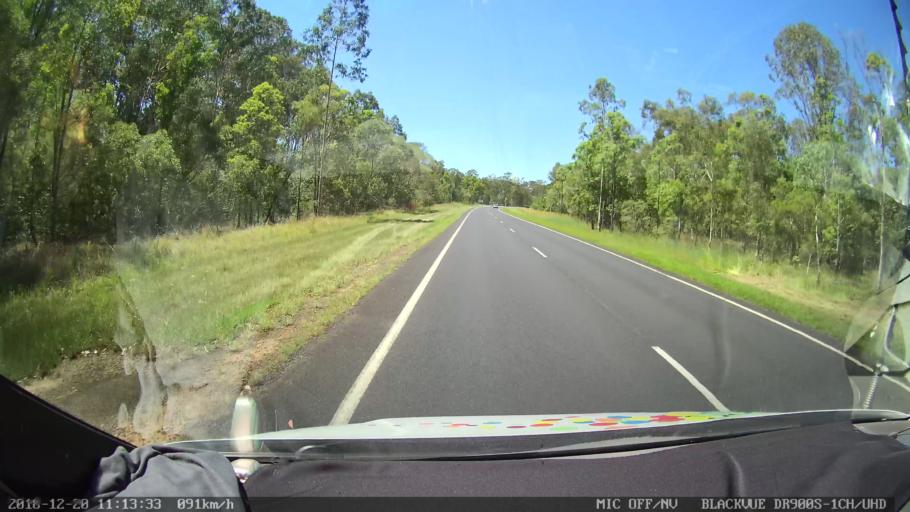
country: AU
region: New South Wales
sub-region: Richmond Valley
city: Casino
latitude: -28.9891
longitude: 153.0110
